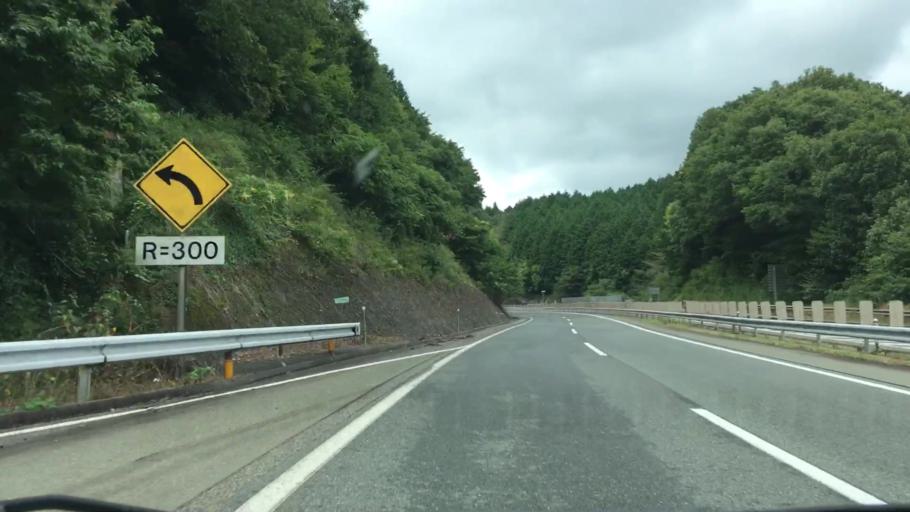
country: JP
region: Hiroshima
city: Shobara
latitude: 34.8911
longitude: 133.2211
